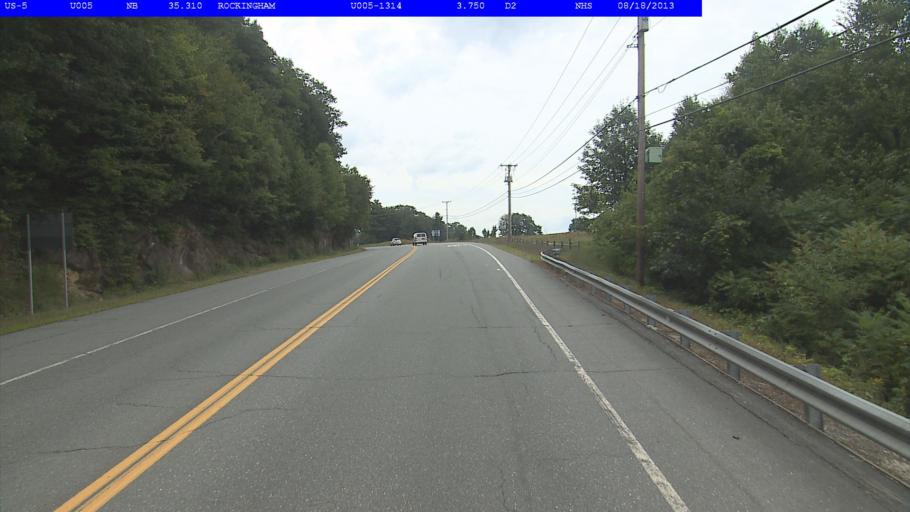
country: US
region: Vermont
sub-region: Windham County
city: Rockingham
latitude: 43.1750
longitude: -72.4592
